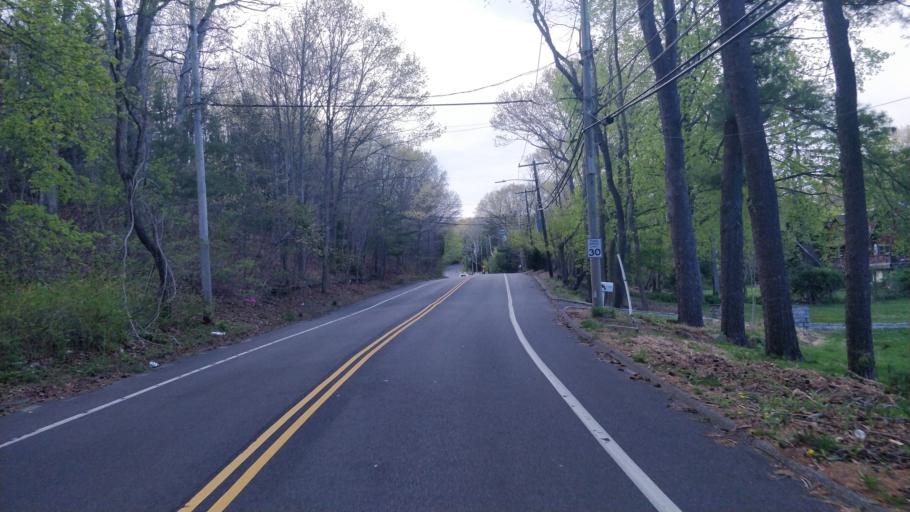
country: US
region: New York
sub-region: Suffolk County
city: Smithtown
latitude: 40.8729
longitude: -73.2086
